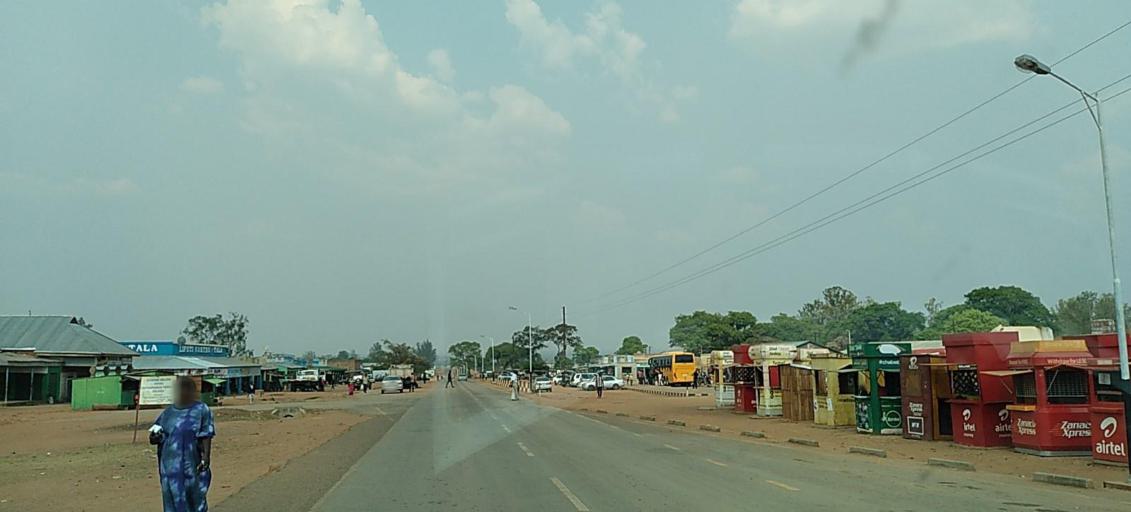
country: ZM
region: North-Western
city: Kabompo
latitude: -13.5939
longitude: 24.2002
